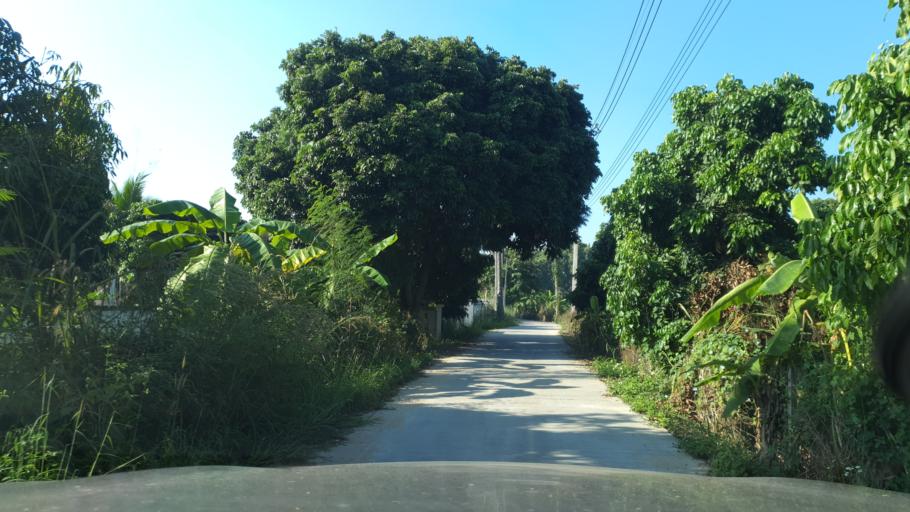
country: TH
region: Chiang Mai
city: San Kamphaeng
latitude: 18.6880
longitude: 99.1432
